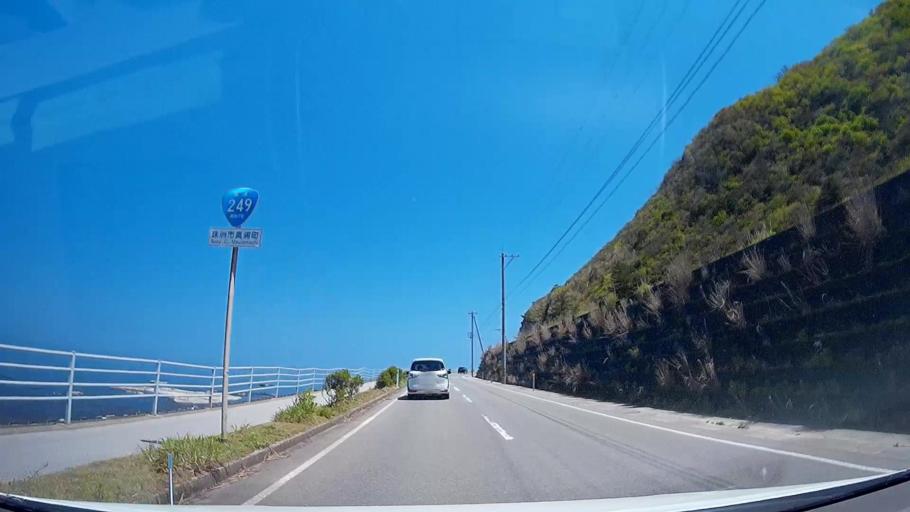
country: JP
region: Ishikawa
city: Nanao
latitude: 37.4787
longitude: 137.1005
